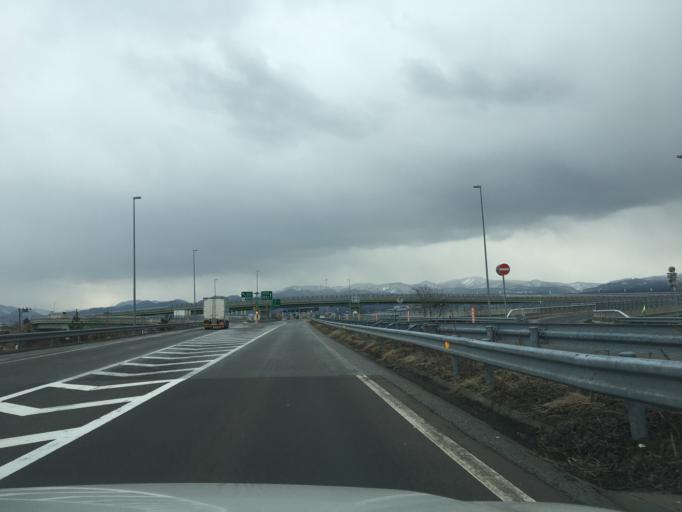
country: JP
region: Aomori
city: Aomori Shi
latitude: 40.7967
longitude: 140.7402
